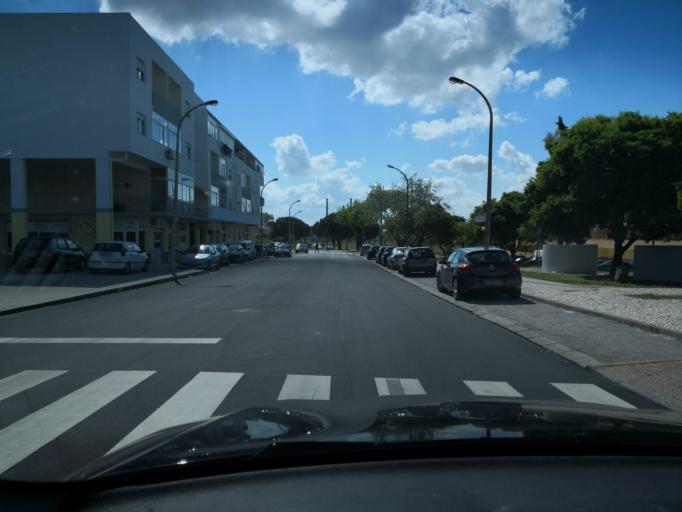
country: PT
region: Setubal
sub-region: Setubal
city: Setubal
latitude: 38.5226
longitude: -8.8665
